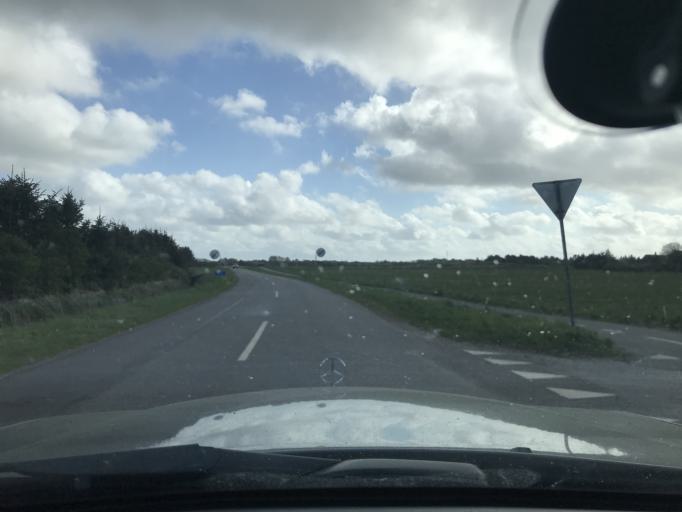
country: DE
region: Schleswig-Holstein
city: List
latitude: 55.1736
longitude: 8.5566
